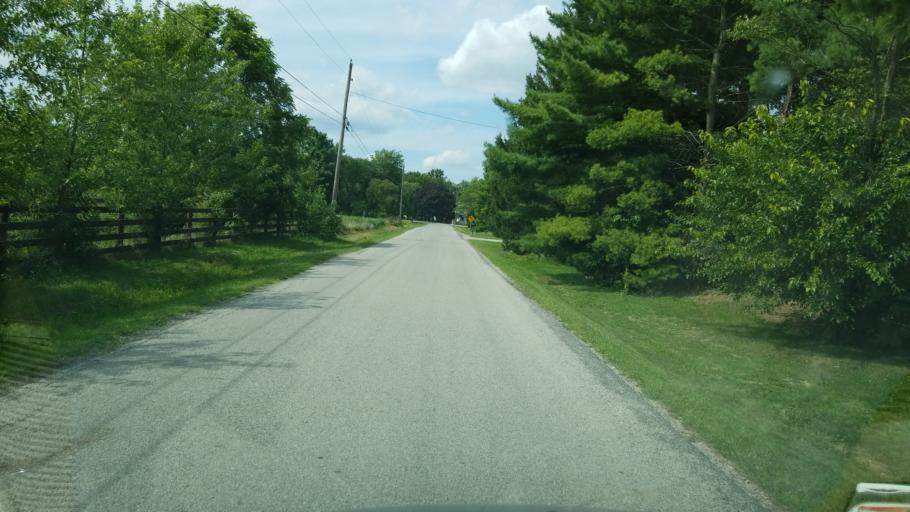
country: US
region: Ohio
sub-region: Marion County
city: Marion
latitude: 40.5292
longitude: -83.0924
